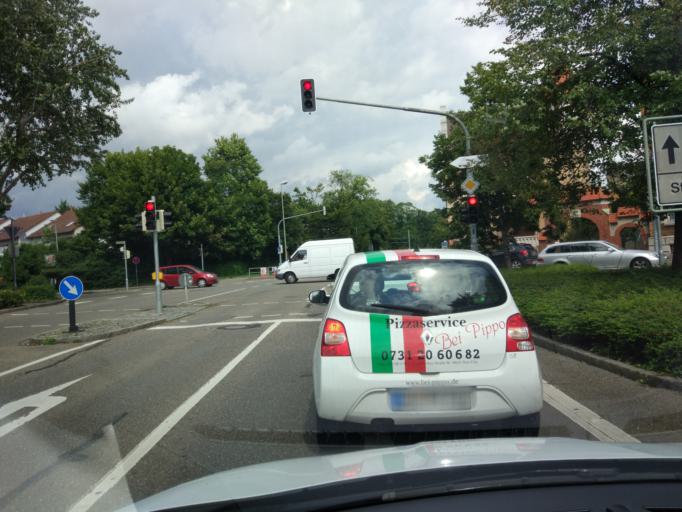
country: DE
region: Bavaria
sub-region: Swabia
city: Neu-Ulm
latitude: 48.4070
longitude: 10.0069
